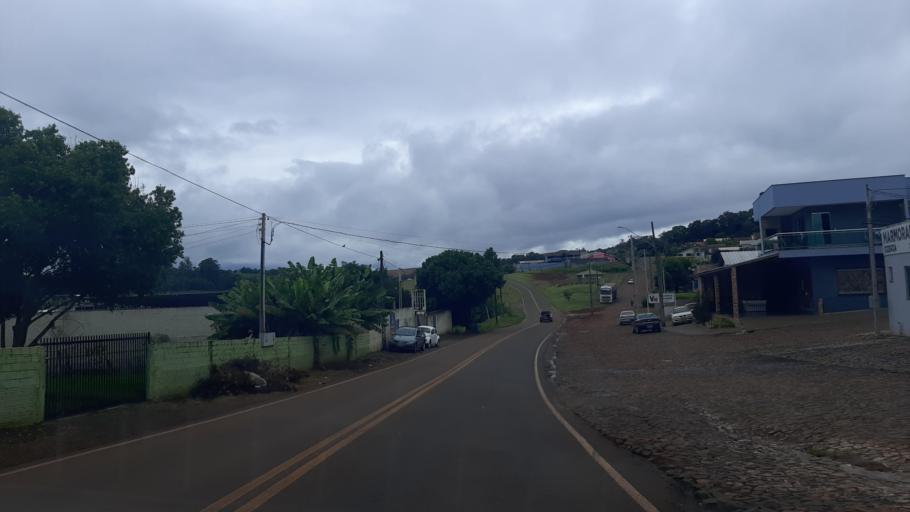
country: BR
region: Parana
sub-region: Ampere
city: Ampere
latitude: -25.9280
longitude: -53.4668
